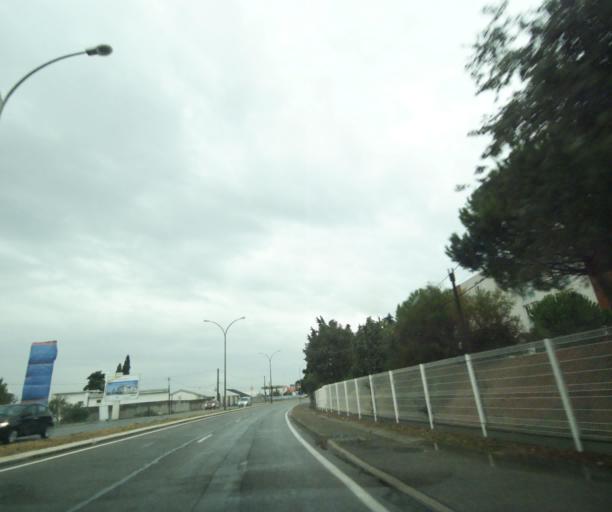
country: FR
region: Languedoc-Roussillon
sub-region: Departement du Gard
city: Rodilhan
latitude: 43.8506
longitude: 4.4003
